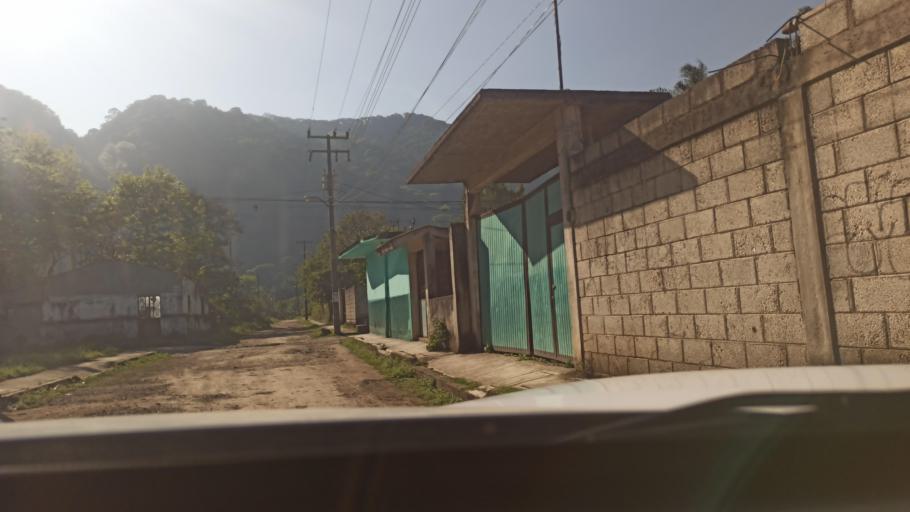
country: MX
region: Veracruz
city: Atzacan
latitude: 18.9098
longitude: -97.0884
